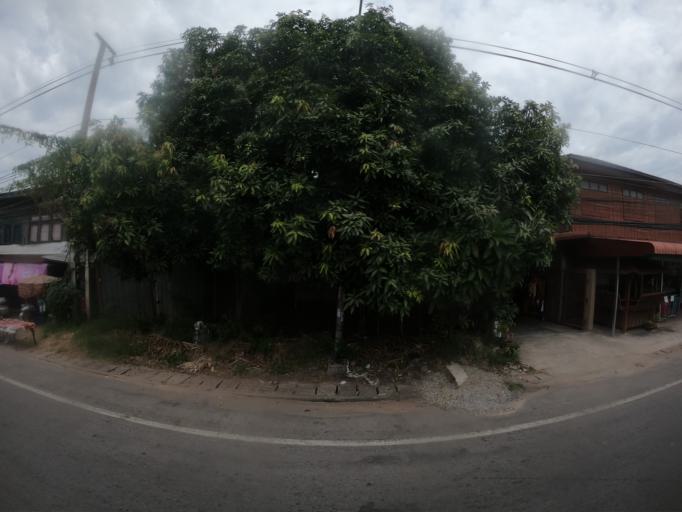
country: TH
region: Maha Sarakham
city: Maha Sarakham
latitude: 16.1739
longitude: 103.3173
